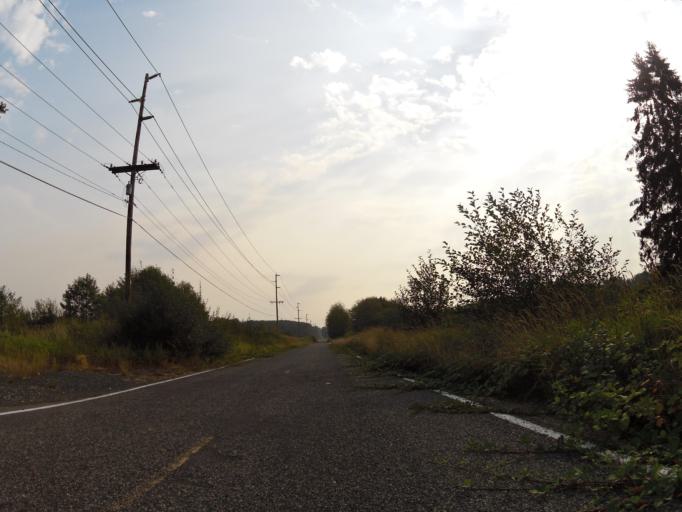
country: US
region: Washington
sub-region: Whatcom County
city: Birch Bay
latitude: 48.8777
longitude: -122.7340
